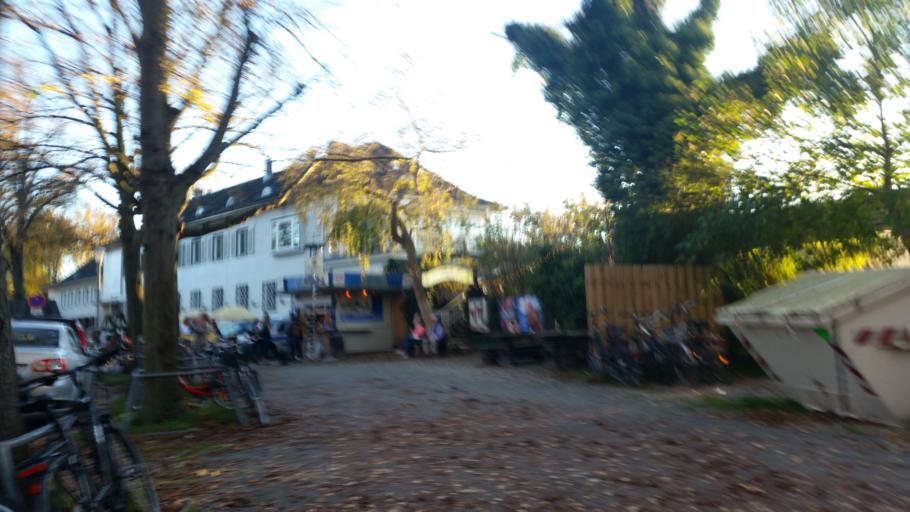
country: DE
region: Lower Saxony
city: Hannover
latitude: 52.3439
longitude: 9.7549
